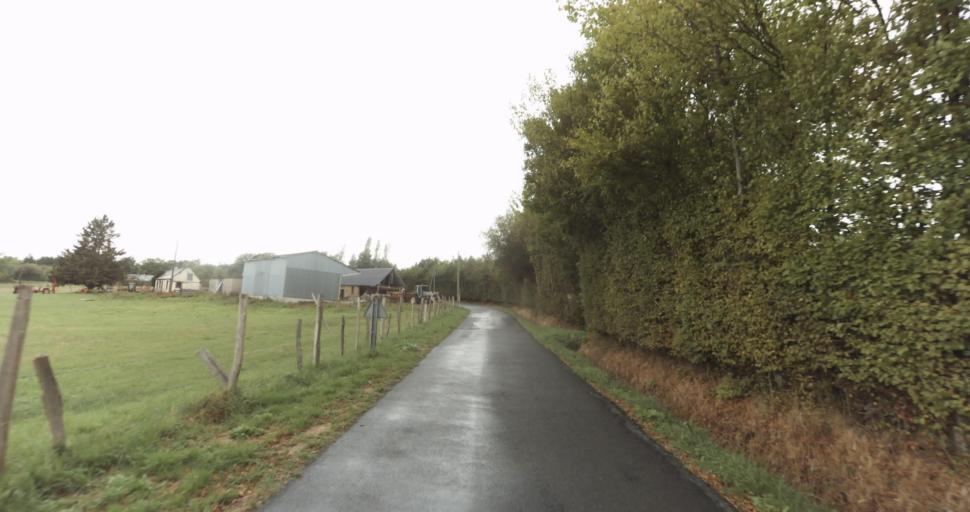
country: FR
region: Lower Normandy
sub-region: Departement de l'Orne
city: Sainte-Gauburge-Sainte-Colombe
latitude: 48.7507
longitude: 0.4703
